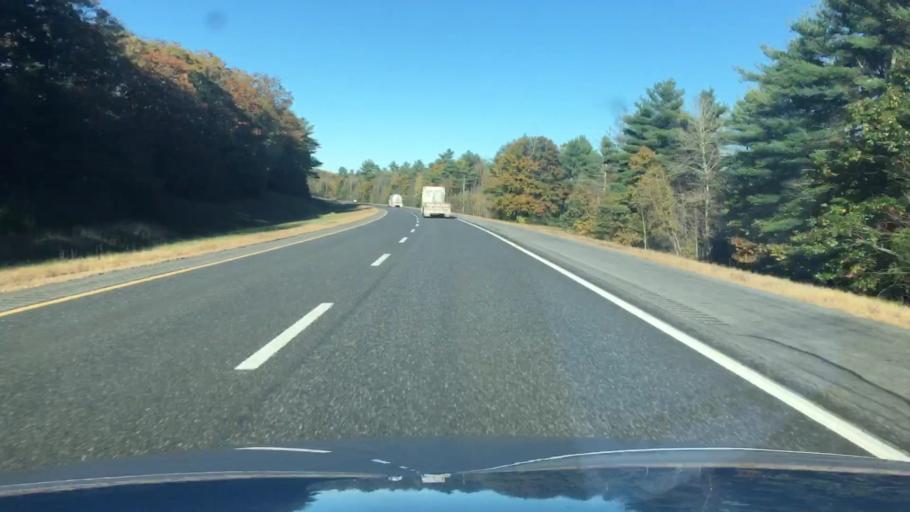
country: US
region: Maine
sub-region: Sagadahoc County
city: Topsham
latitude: 44.0037
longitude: -69.9259
